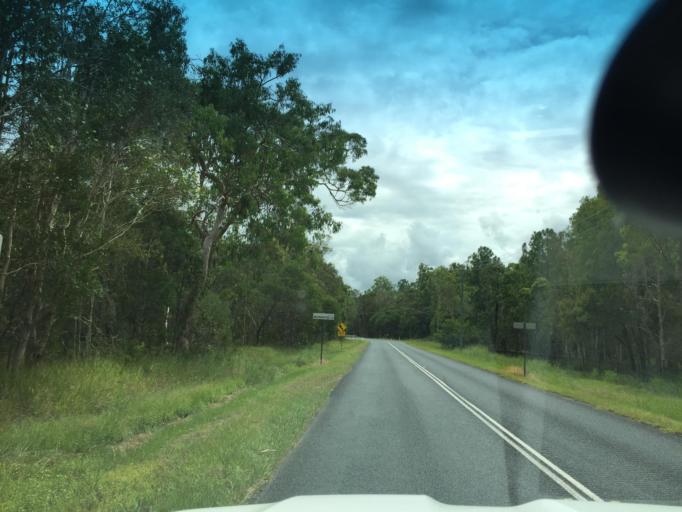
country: AU
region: Queensland
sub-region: Moreton Bay
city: Morayfield
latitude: -27.1218
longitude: 152.9783
